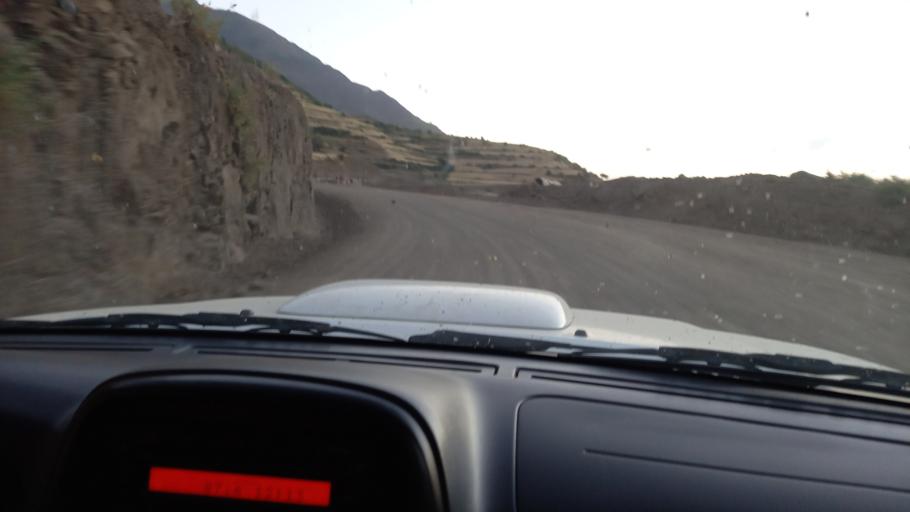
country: ET
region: Amhara
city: Debark'
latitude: 13.0367
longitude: 38.0556
